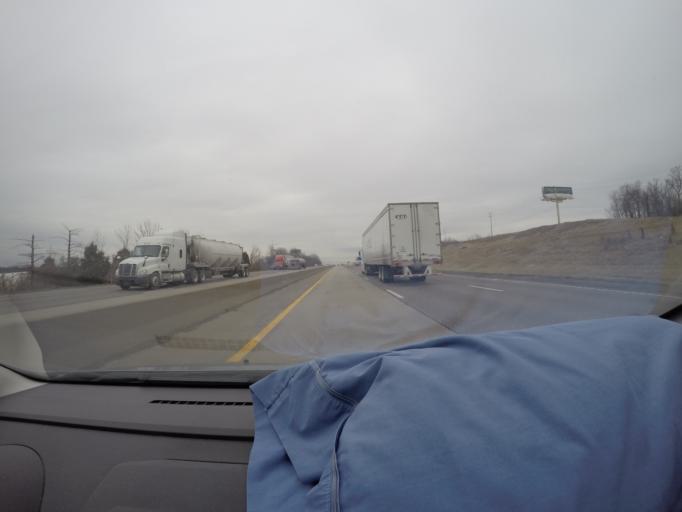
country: US
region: Missouri
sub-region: Saint Charles County
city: Dardenne Prairie
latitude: 38.8033
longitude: -90.7443
